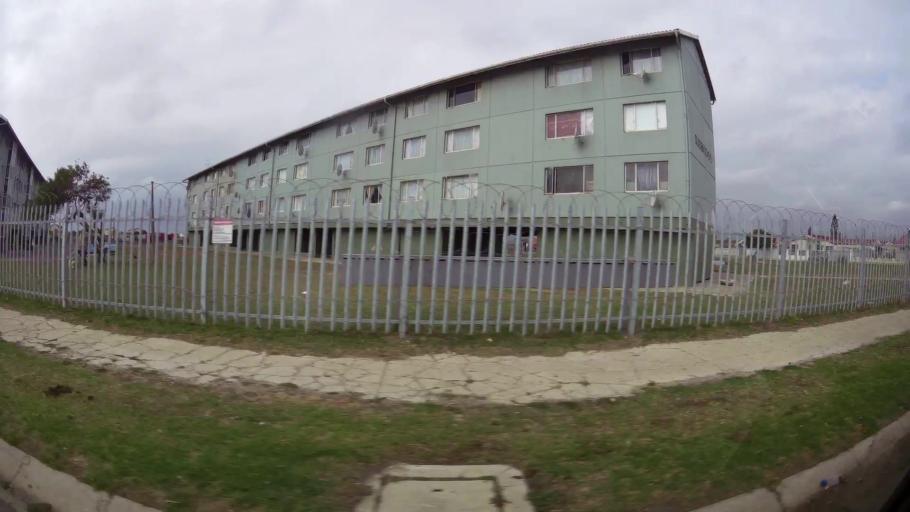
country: ZA
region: Eastern Cape
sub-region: Nelson Mandela Bay Metropolitan Municipality
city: Port Elizabeth
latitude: -33.8952
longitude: 25.5527
